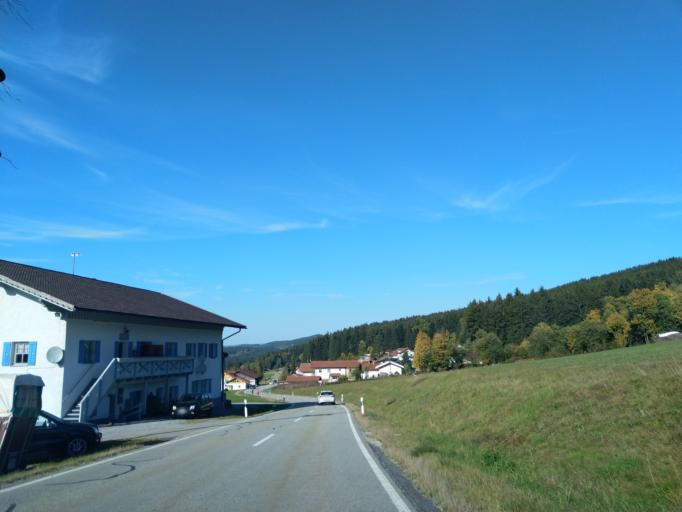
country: DE
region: Bavaria
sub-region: Lower Bavaria
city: Achslach
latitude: 48.9450
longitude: 12.9249
